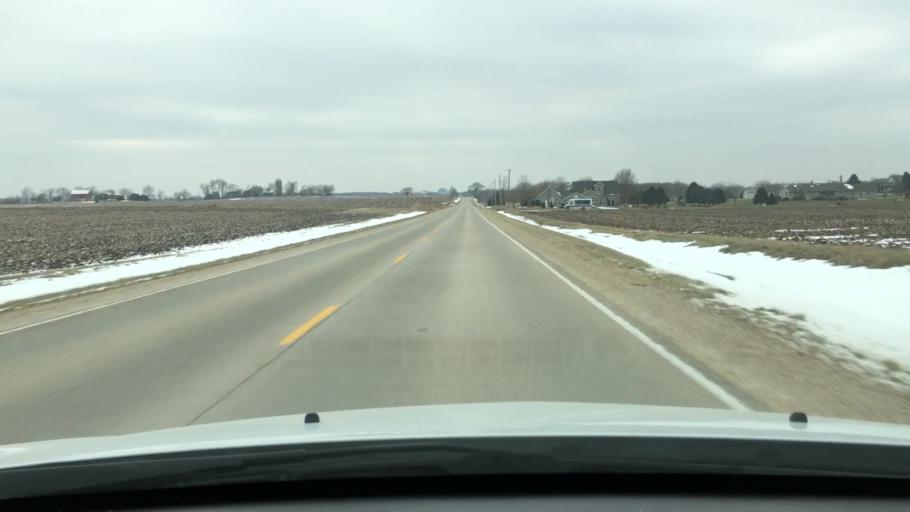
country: US
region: Illinois
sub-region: Ogle County
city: Rochelle
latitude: 41.8479
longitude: -88.9685
